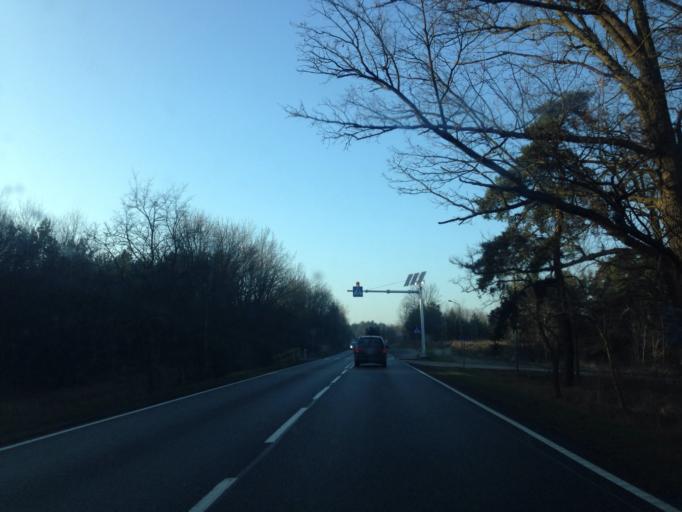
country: PL
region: Kujawsko-Pomorskie
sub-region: Powiat torunski
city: Zlawies Wielka
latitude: 53.0522
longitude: 18.3282
